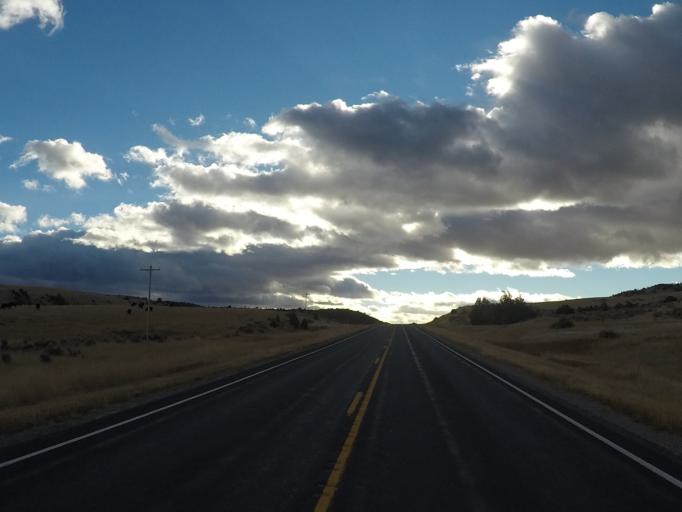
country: US
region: Montana
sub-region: Jefferson County
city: Whitehall
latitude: 45.9119
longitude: -111.9388
